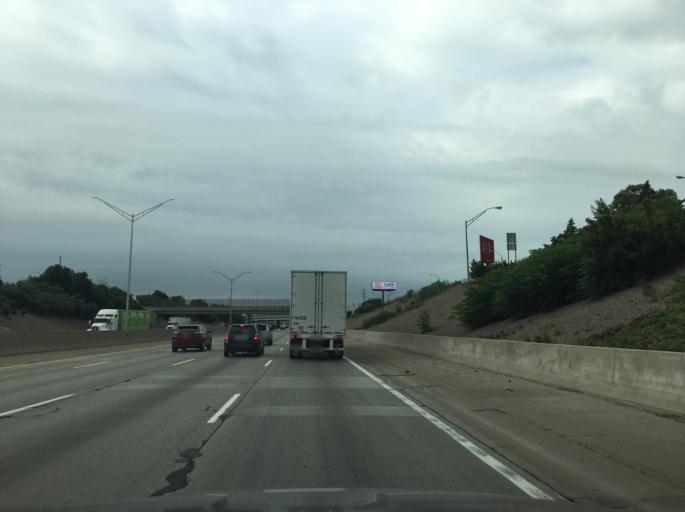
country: US
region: Michigan
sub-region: Oakland County
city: Madison Heights
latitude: 42.4871
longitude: -83.0828
